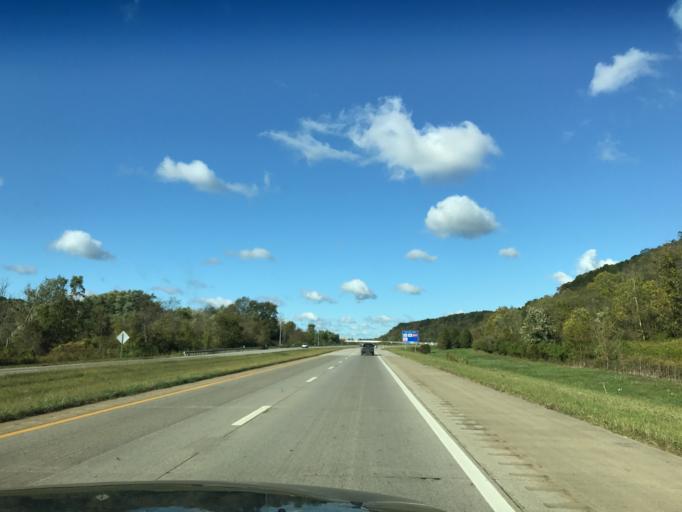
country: US
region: Ohio
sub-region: Athens County
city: Athens
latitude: 39.3343
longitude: -82.0209
